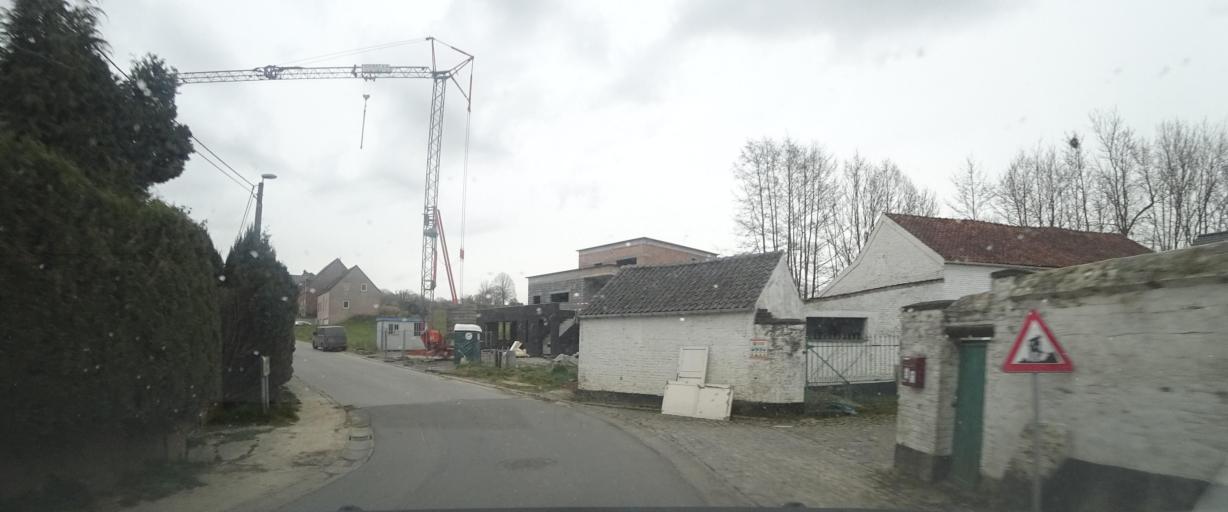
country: BE
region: Wallonia
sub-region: Province du Brabant Wallon
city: Mont-Saint-Guibert
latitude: 50.6305
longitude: 4.6057
